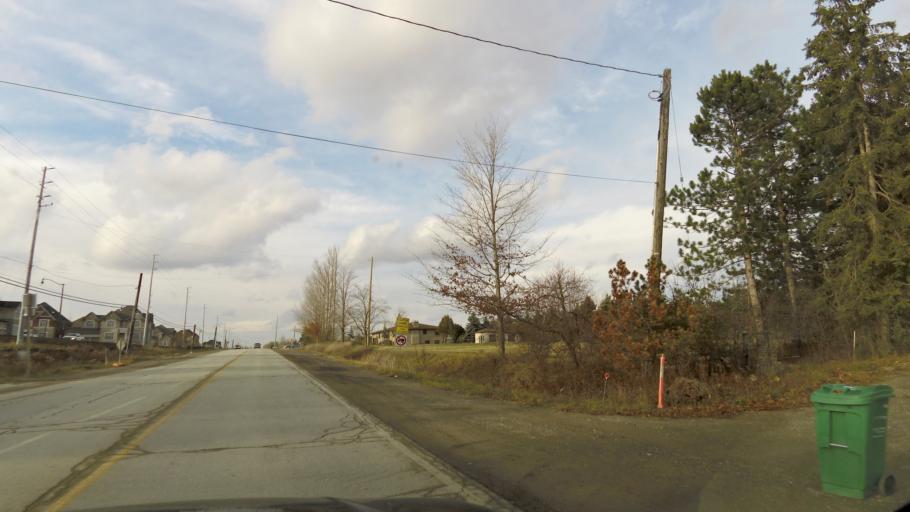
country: CA
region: Ontario
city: Brampton
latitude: 43.8121
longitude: -79.7172
